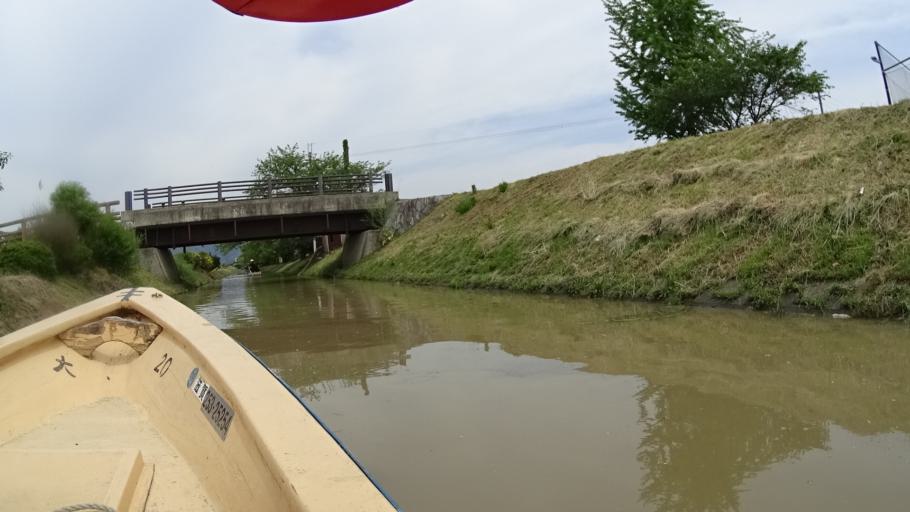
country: JP
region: Shiga Prefecture
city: Omihachiman
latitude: 35.1514
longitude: 136.1017
